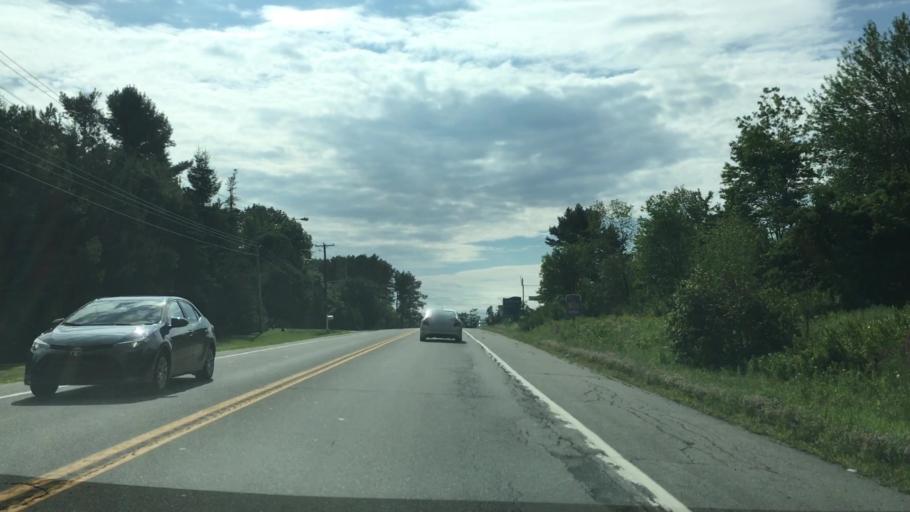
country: US
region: Maine
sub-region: Waldo County
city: Belfast
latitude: 44.4312
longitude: -68.9625
